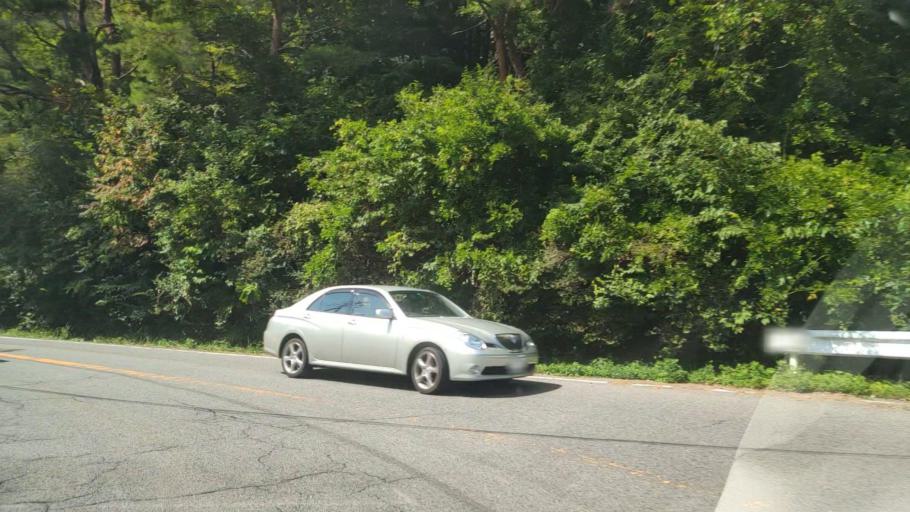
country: JP
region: Gunma
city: Shibukawa
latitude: 36.4999
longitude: 138.9056
